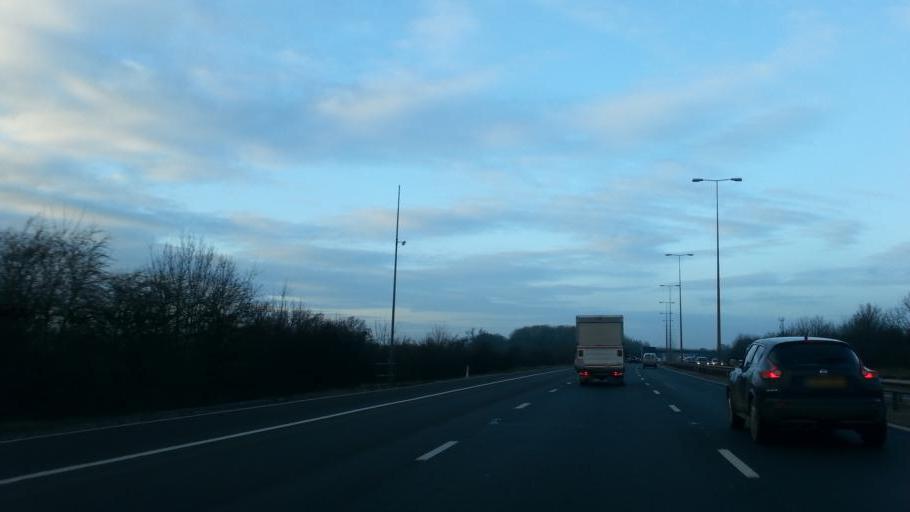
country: GB
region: England
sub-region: Worcestershire
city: Kempsey
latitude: 52.1040
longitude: -2.1903
